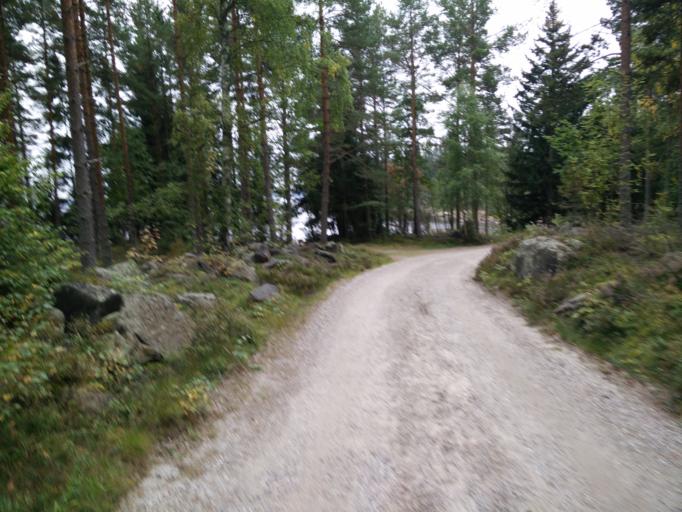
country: SE
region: Gaevleborg
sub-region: Hudiksvalls Kommun
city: Hudiksvall
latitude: 61.8337
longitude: 17.3390
